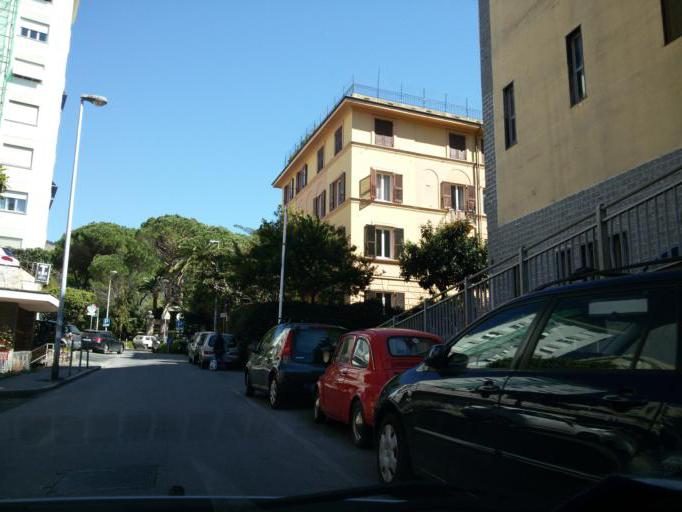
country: IT
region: Liguria
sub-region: Provincia di Genova
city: Bogliasco
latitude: 44.3889
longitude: 8.9994
